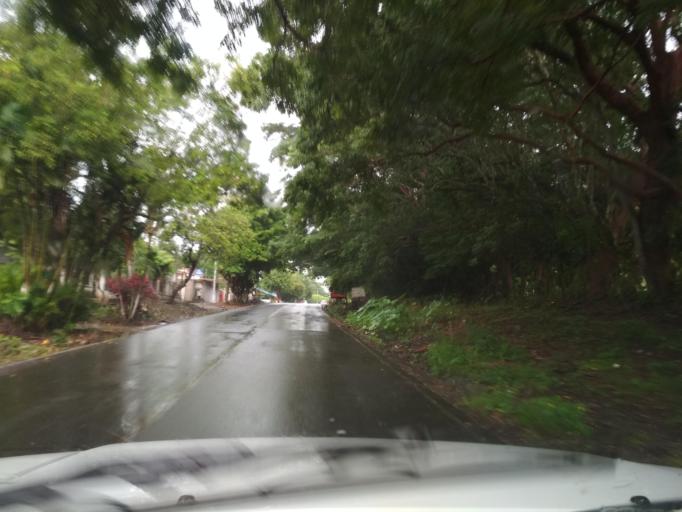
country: MX
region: Veracruz
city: Santiago Tuxtla
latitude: 18.4498
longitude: -95.3157
